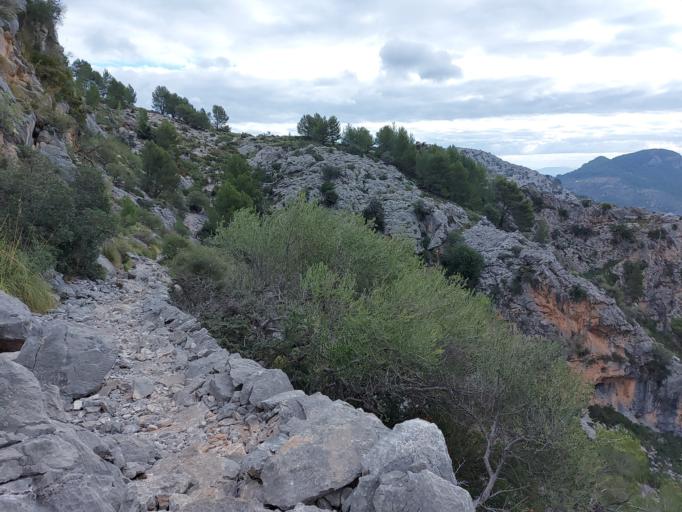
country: ES
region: Balearic Islands
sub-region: Illes Balears
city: Mancor de la Vall
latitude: 39.7714
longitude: 2.8113
